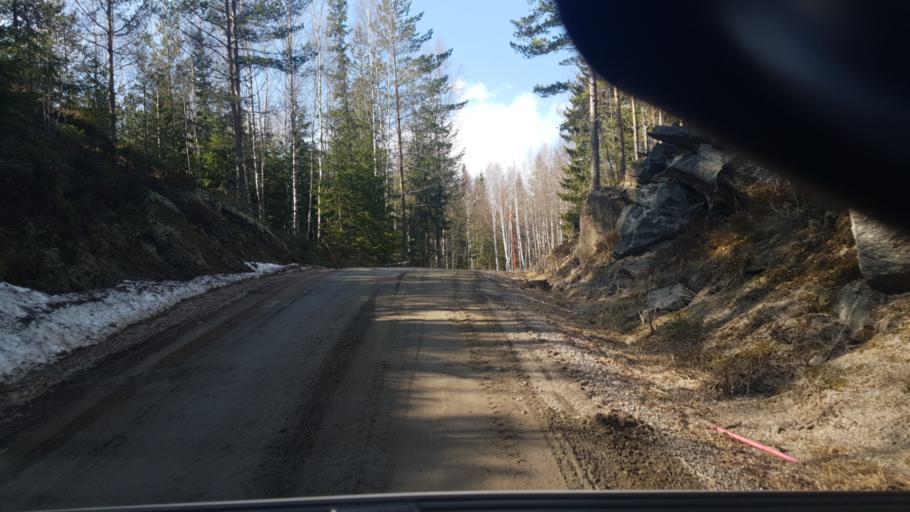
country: SE
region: Vaermland
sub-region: Eda Kommun
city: Amotfors
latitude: 59.8265
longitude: 12.4025
